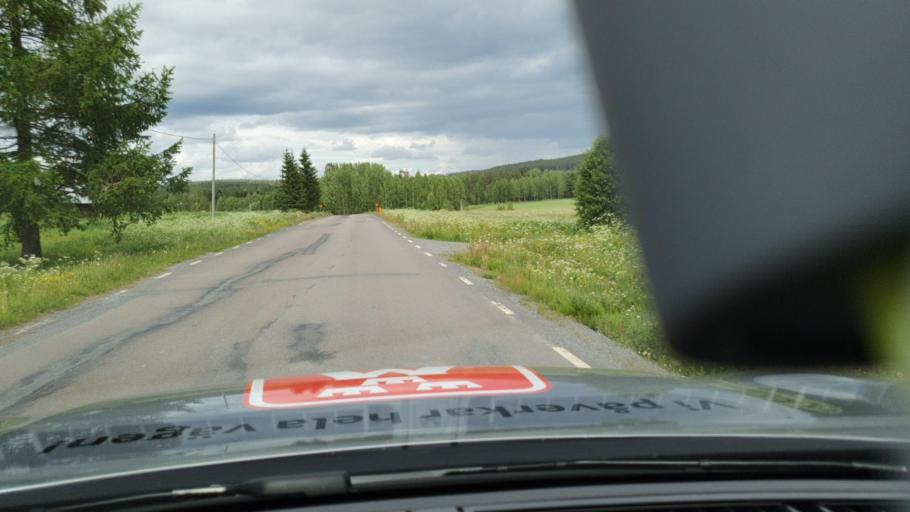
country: SE
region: Norrbotten
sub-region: Lulea Kommun
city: Sodra Sunderbyn
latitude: 65.8513
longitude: 21.9220
